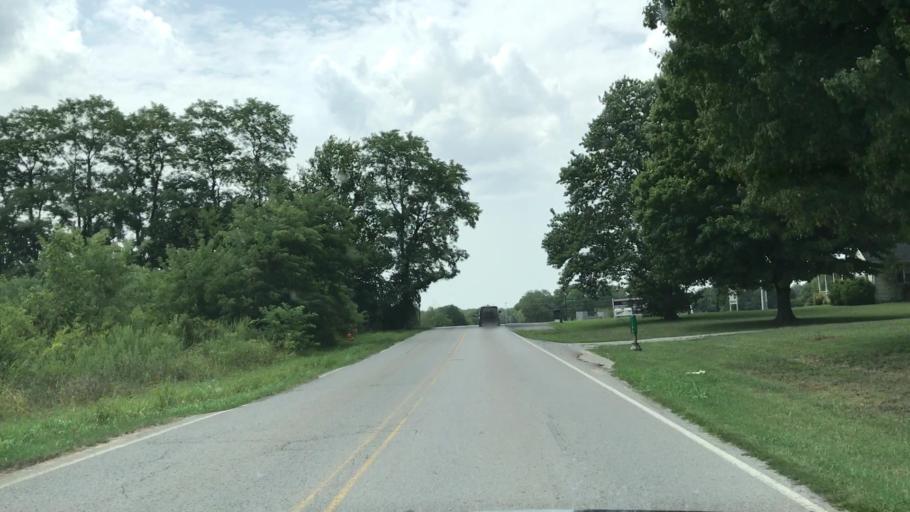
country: US
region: Tennessee
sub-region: Rutherford County
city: La Vergne
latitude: 35.9665
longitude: -86.6037
